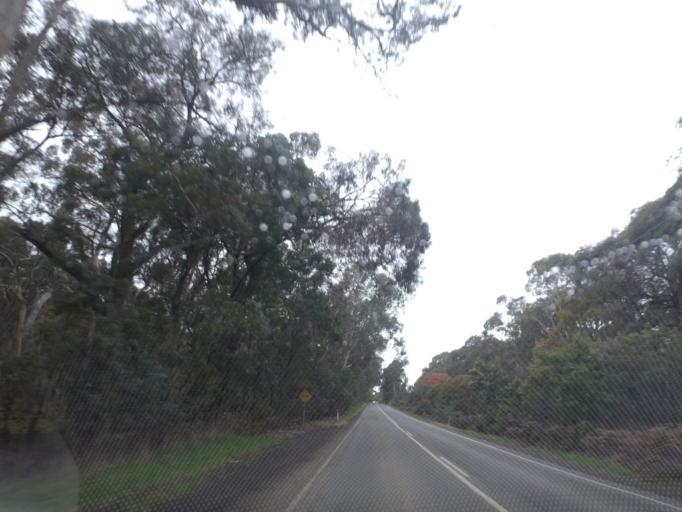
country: AU
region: Victoria
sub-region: Hume
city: Sunbury
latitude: -37.3451
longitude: 144.6772
